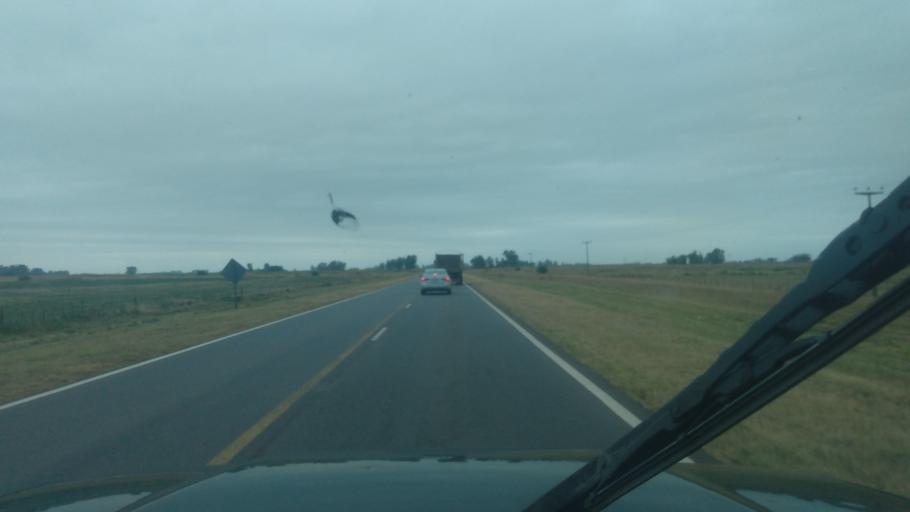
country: AR
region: Buenos Aires
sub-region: Partido de Nueve de Julio
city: Nueve de Julio
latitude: -35.3991
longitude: -60.7589
